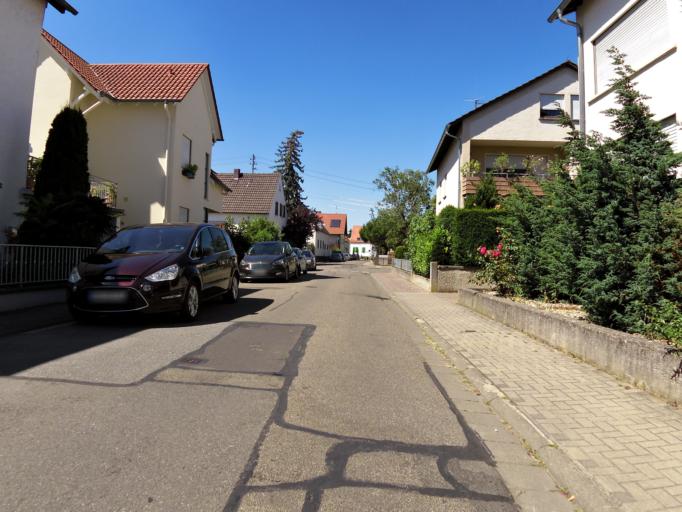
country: DE
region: Rheinland-Pfalz
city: Niederkirchen bei Deidesheim
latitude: 49.4110
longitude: 8.2114
